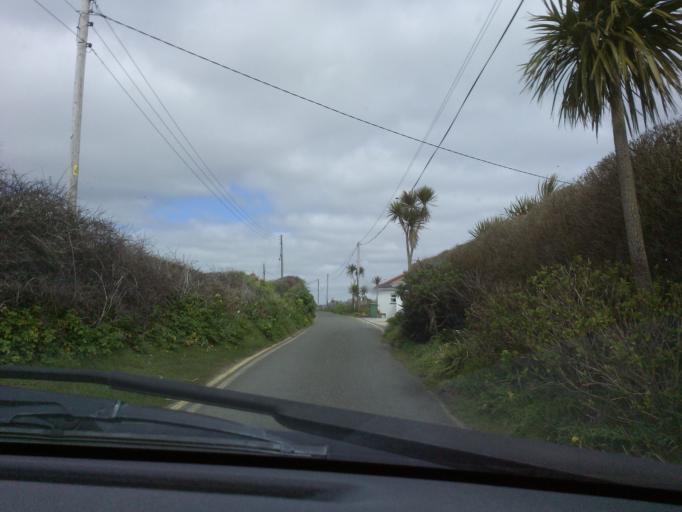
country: GB
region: England
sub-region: Cornwall
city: St. Buryan
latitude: 50.0418
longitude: -5.6555
